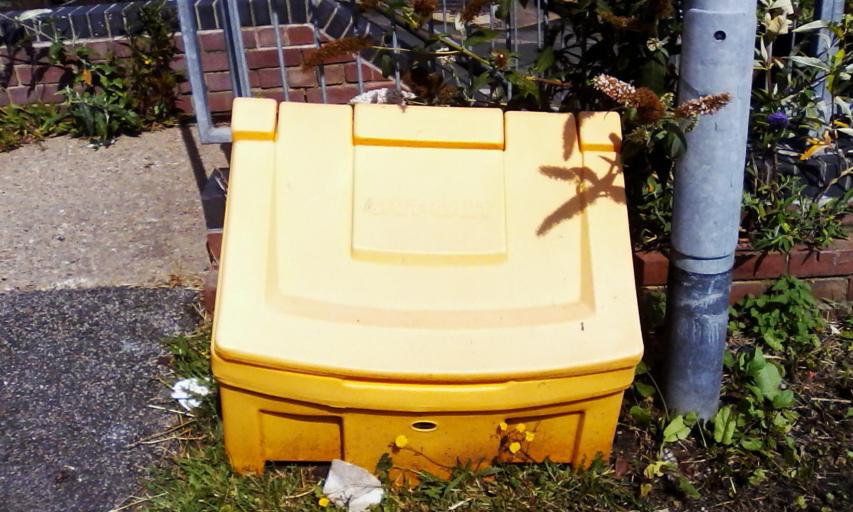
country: GB
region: England
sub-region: Nottinghamshire
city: Arnold
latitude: 52.9784
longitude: -1.1081
